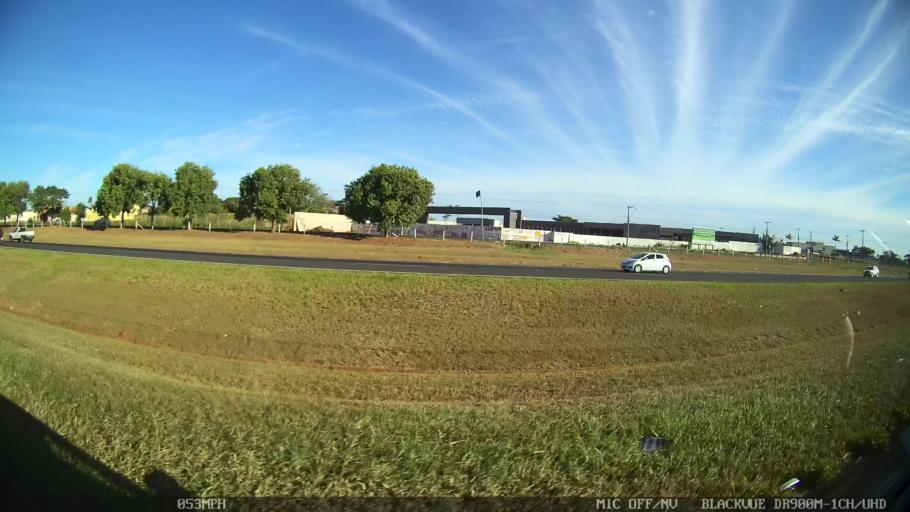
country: BR
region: Sao Paulo
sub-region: Sao Jose Do Rio Preto
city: Sao Jose do Rio Preto
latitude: -20.8238
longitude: -49.4148
